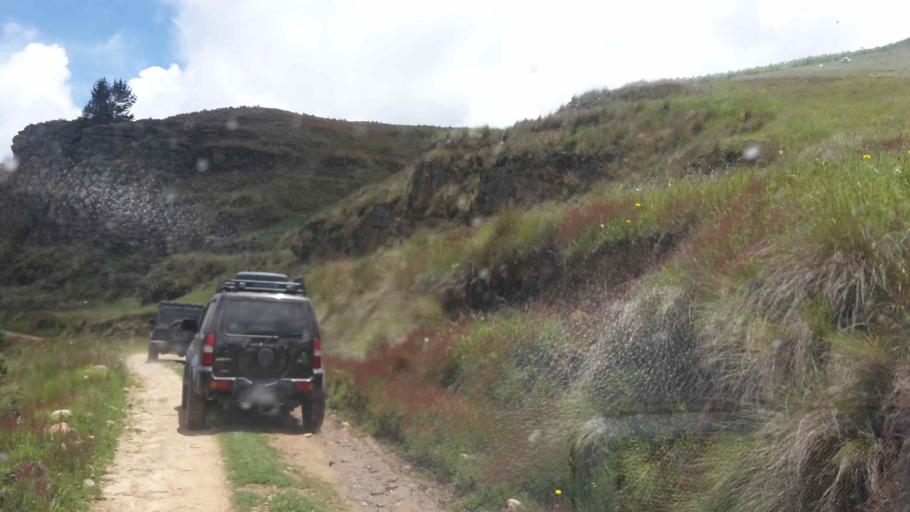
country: BO
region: Cochabamba
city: Cochabamba
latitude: -17.1877
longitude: -66.0697
